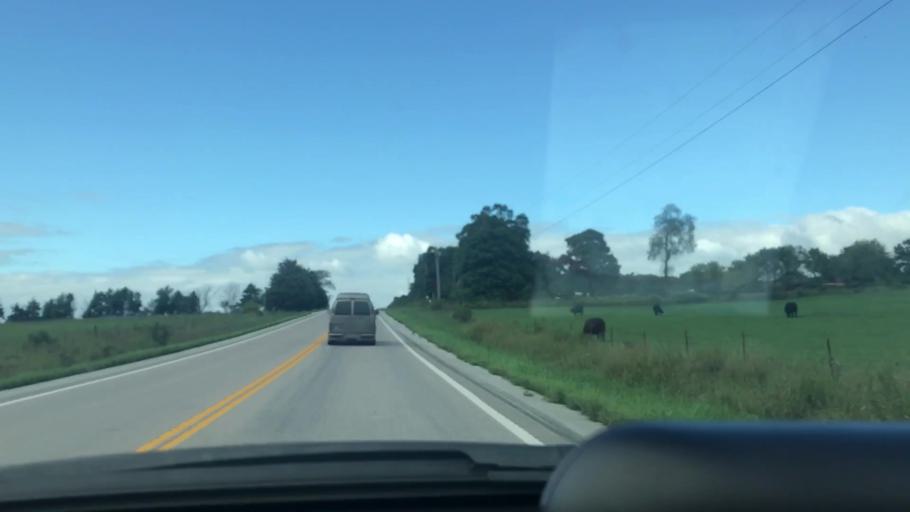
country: US
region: Missouri
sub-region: Hickory County
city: Hermitage
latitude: 37.9615
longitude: -93.2069
